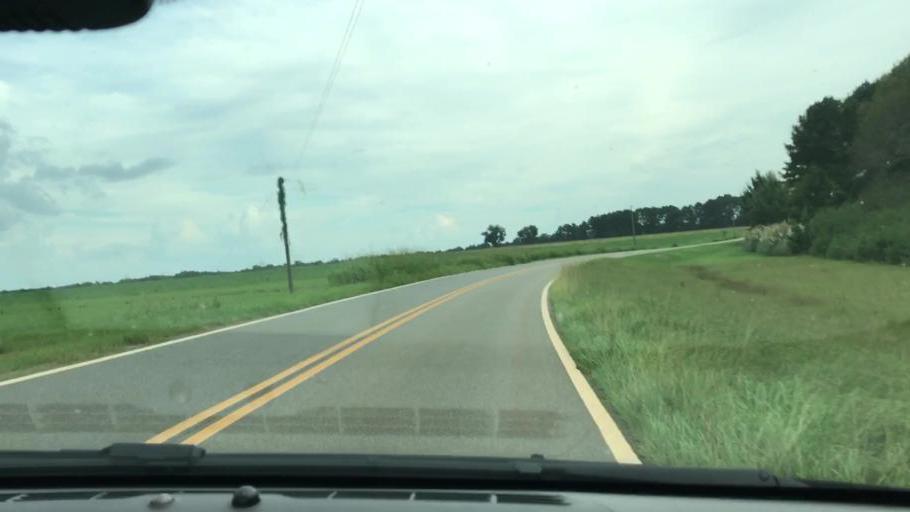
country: US
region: Georgia
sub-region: Early County
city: Blakely
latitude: 31.4523
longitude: -84.9134
